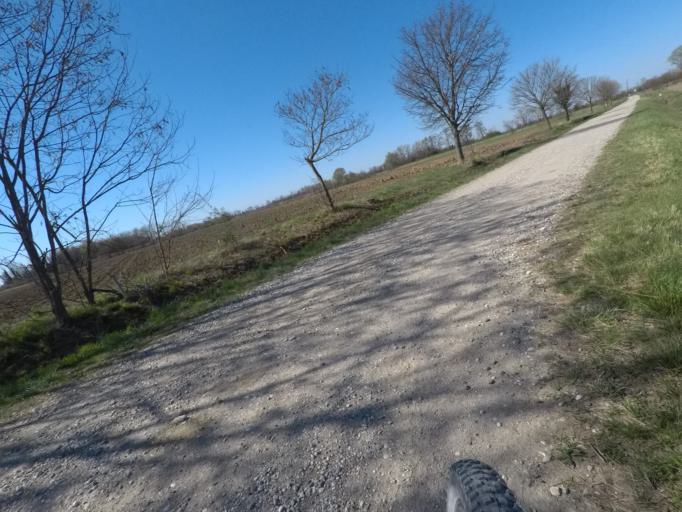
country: IT
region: Friuli Venezia Giulia
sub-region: Provincia di Udine
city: Moimacco
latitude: 46.0907
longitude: 13.3564
